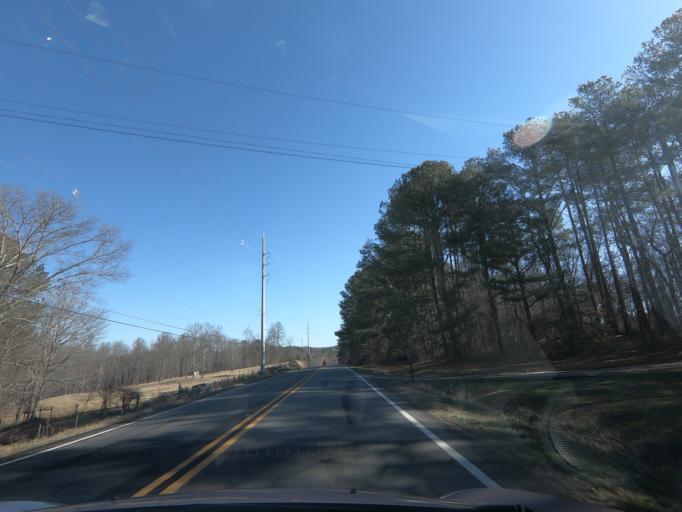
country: US
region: Georgia
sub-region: Dawson County
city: Dawsonville
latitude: 34.3501
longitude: -84.1051
